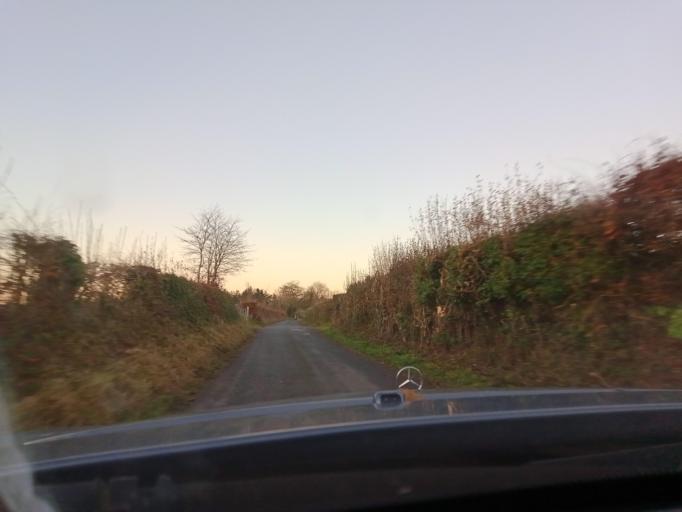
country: IE
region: Leinster
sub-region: Kilkenny
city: Thomastown
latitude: 52.4449
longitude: -7.1054
